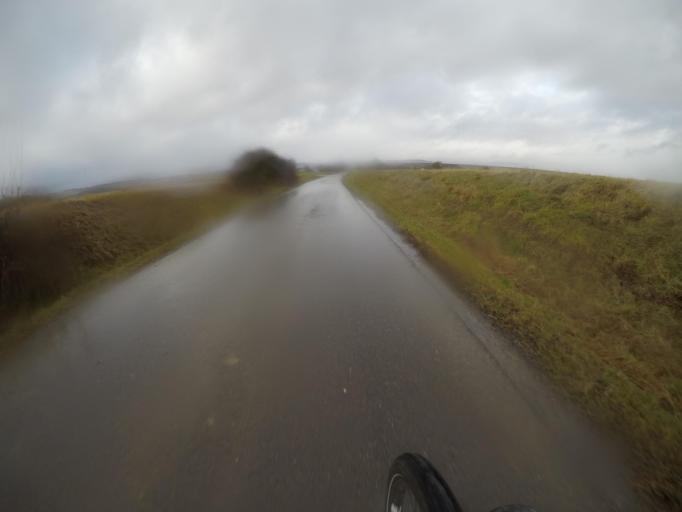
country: DE
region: Baden-Wuerttemberg
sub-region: Regierungsbezirk Stuttgart
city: Eberdingen
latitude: 48.9045
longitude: 8.9965
